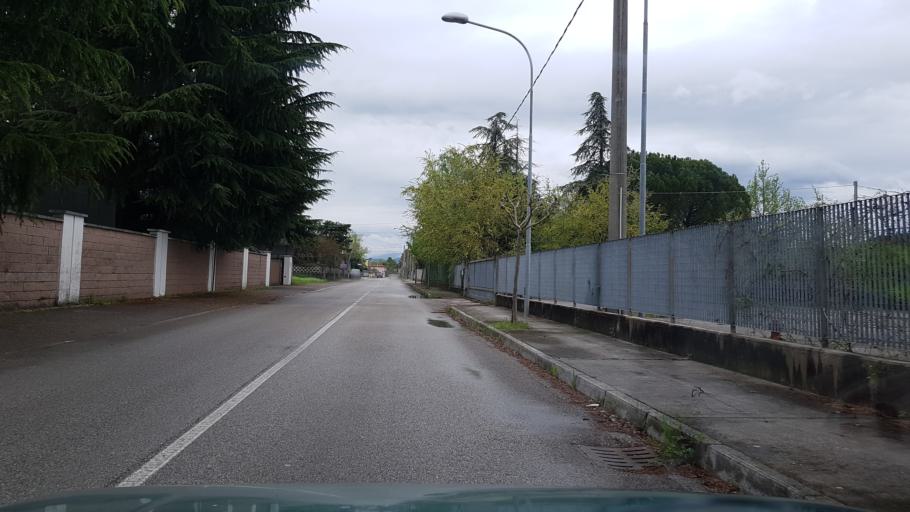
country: IT
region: Friuli Venezia Giulia
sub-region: Provincia di Gorizia
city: Mossa
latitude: 45.9310
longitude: 13.5482
